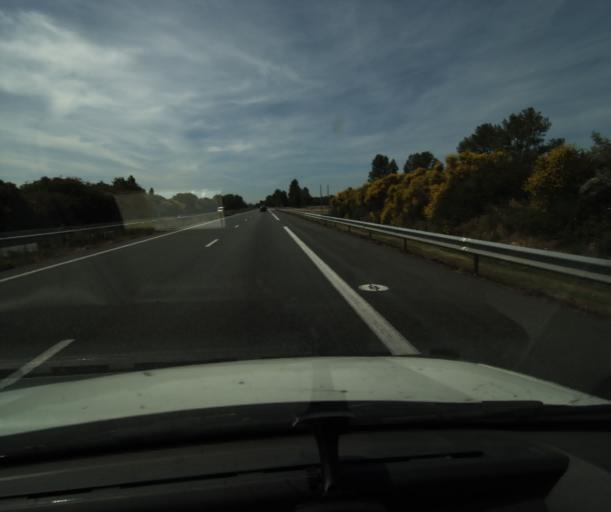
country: FR
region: Languedoc-Roussillon
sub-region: Departement de l'Aude
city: Saint-Martin-Lalande
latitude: 43.2769
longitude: 1.9915
